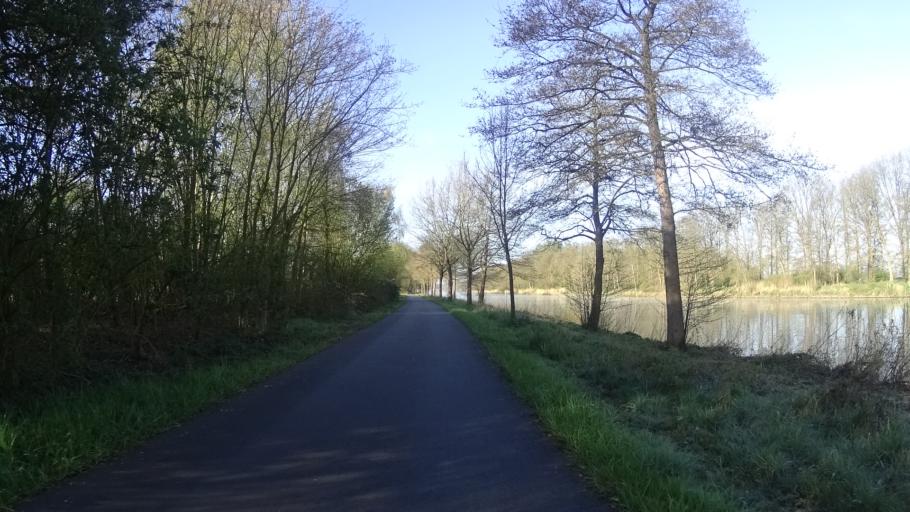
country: DE
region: Lower Saxony
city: Niederlangen
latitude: 52.8453
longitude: 7.2936
